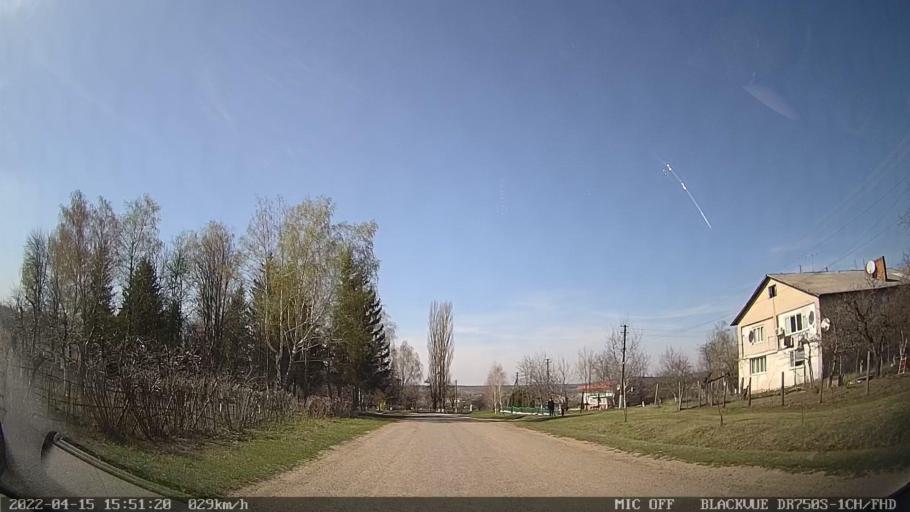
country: MD
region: Raionul Ocnita
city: Otaci
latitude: 48.3940
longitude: 27.8986
